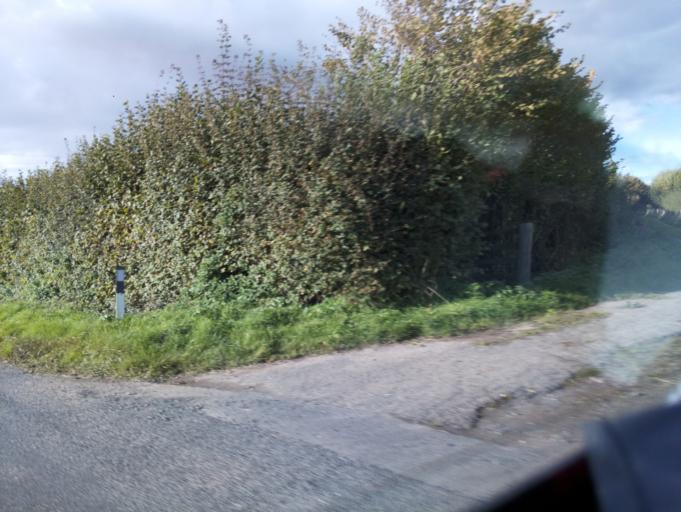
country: GB
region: England
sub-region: Herefordshire
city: Moccas
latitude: 52.0977
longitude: -2.9241
